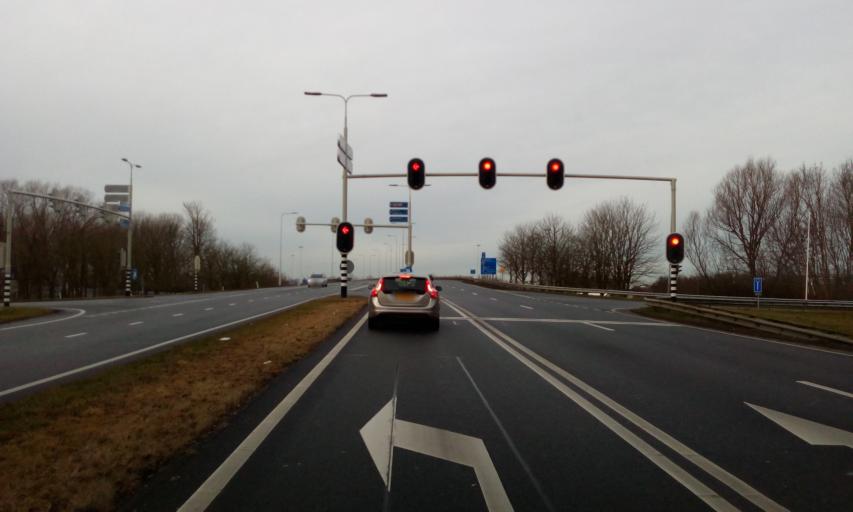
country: NL
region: South Holland
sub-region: Gemeente Gorinchem
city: Gorinchem
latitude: 51.8433
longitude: 4.9442
